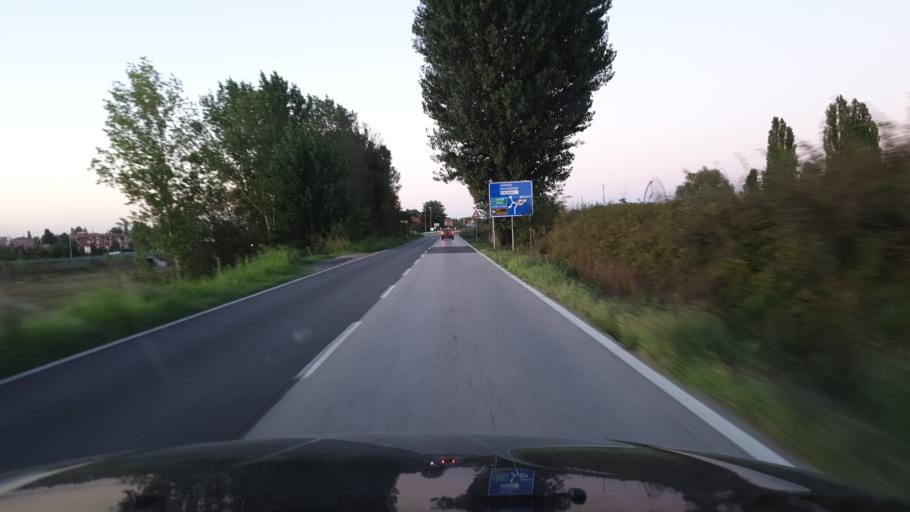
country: IT
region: Emilia-Romagna
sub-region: Provincia di Bologna
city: Altedo
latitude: 44.6584
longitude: 11.4901
